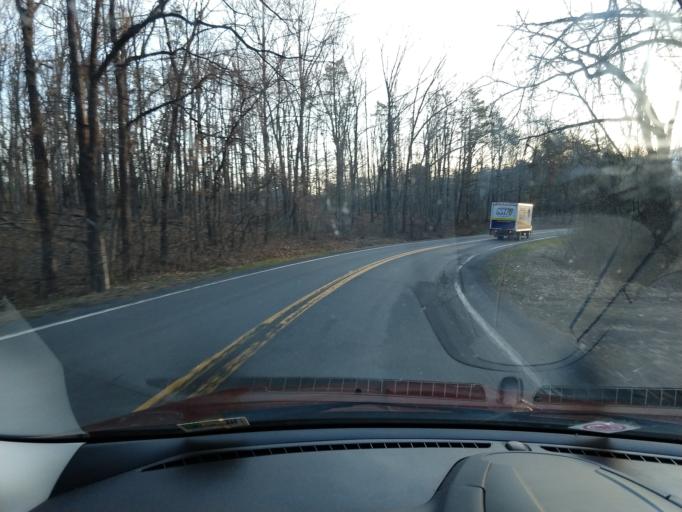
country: US
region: Virginia
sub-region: Frederick County
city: Shawnee Land
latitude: 39.4064
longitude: -78.4400
